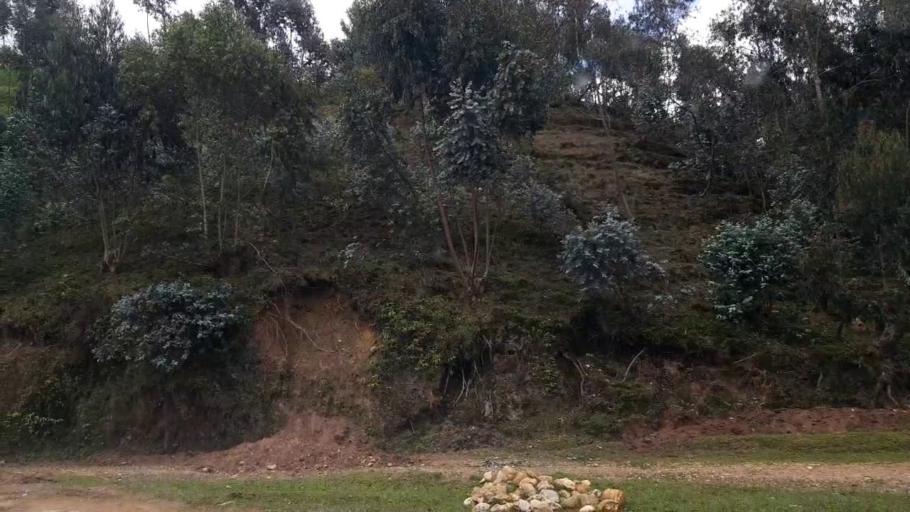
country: RW
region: Western Province
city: Kibuye
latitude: -1.9047
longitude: 29.4551
